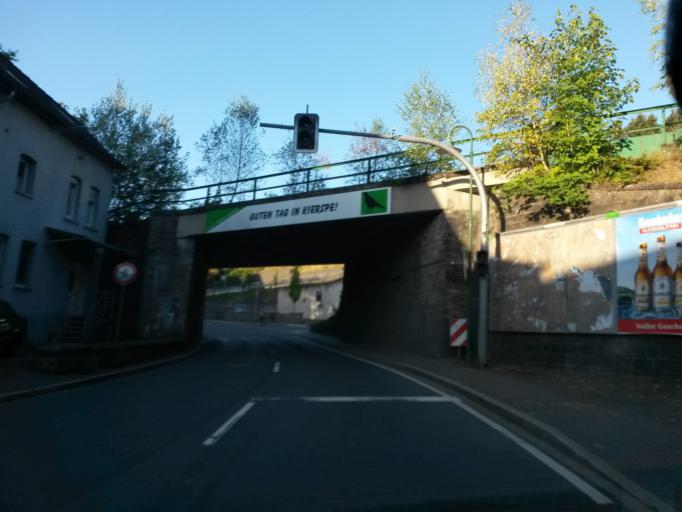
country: DE
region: North Rhine-Westphalia
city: Kierspe
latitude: 51.1290
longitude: 7.6166
